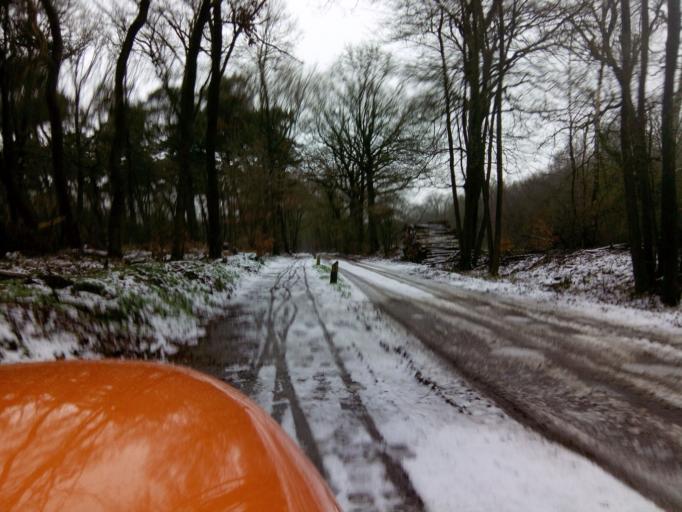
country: NL
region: Gelderland
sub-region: Gemeente Putten
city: Putten
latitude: 52.2277
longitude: 5.5596
